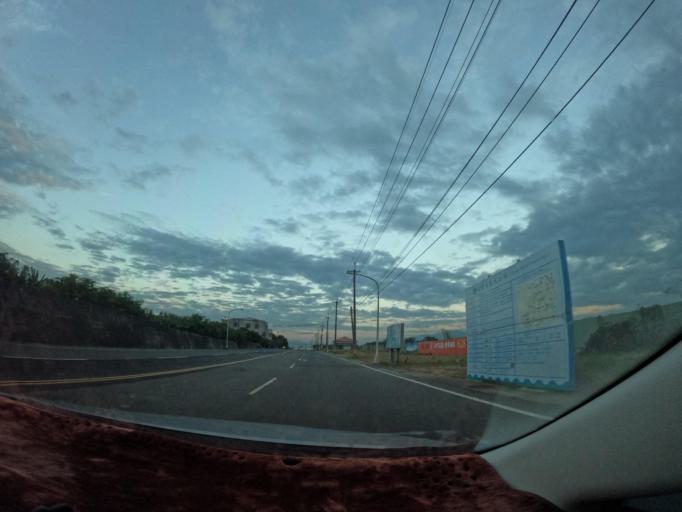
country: TW
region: Taiwan
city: Yujing
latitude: 23.1000
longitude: 120.4457
